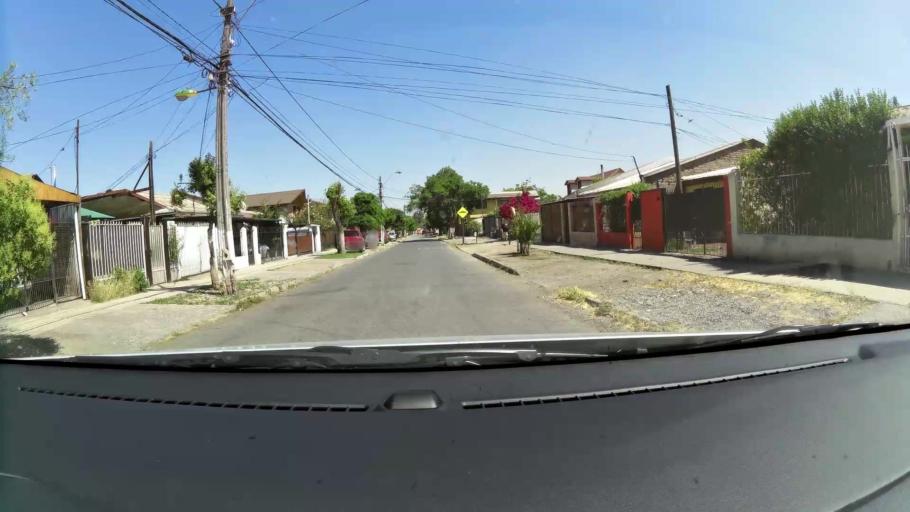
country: CL
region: Santiago Metropolitan
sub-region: Provincia de Maipo
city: San Bernardo
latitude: -33.5609
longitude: -70.6766
